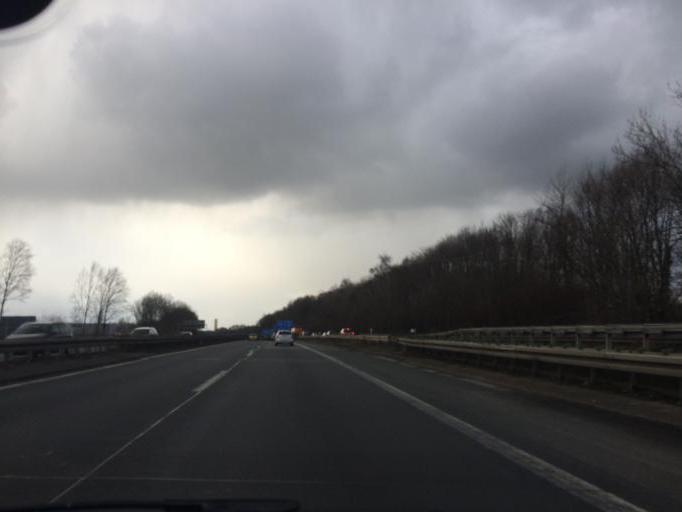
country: DE
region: North Rhine-Westphalia
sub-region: Regierungsbezirk Arnsberg
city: Bochum
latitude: 51.4982
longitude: 7.2692
